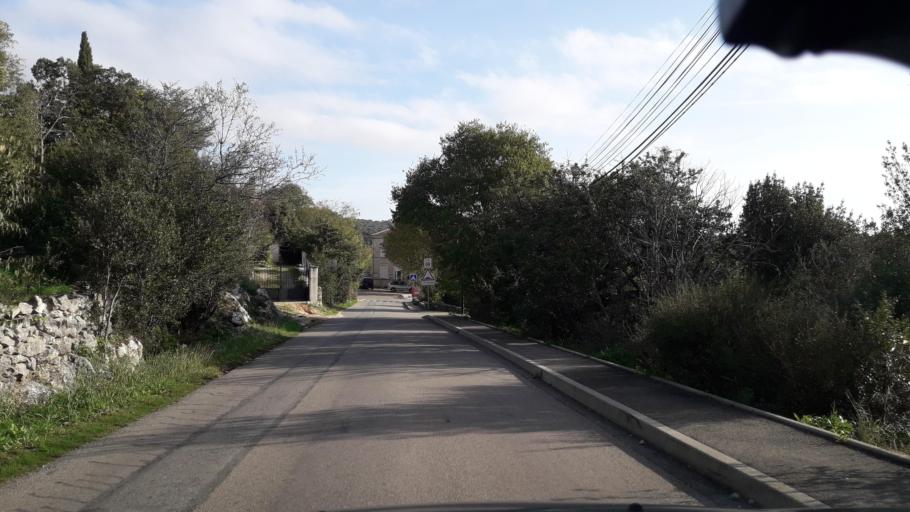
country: FR
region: Languedoc-Roussillon
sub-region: Departement du Gard
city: Saint-Julien-de-Peyrolas
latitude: 44.3656
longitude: 4.5332
